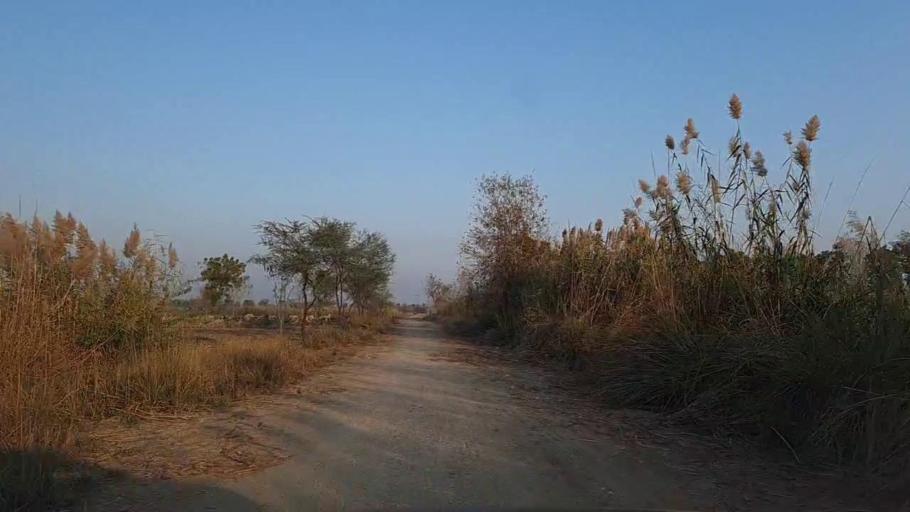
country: PK
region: Sindh
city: Daur
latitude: 26.4873
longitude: 68.4249
